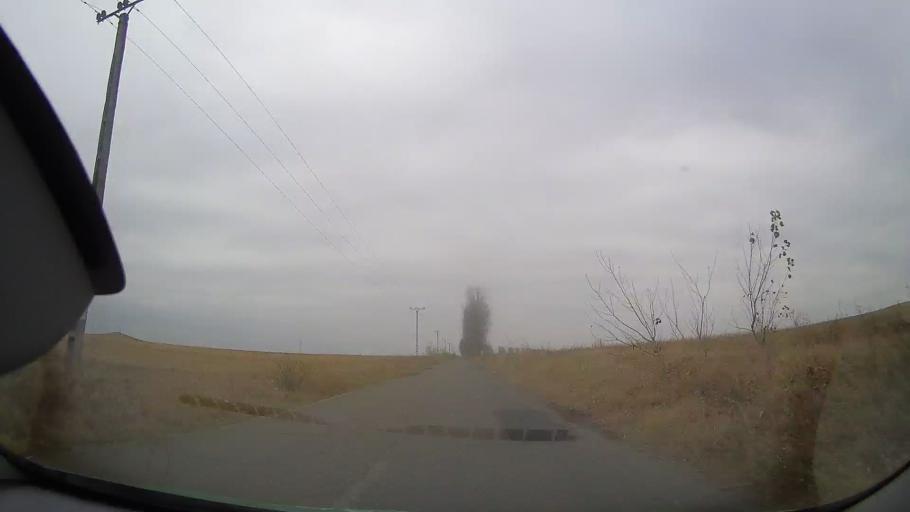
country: RO
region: Buzau
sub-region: Comuna Pogoanele
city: Pogoanele
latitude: 44.9614
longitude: 27.0209
